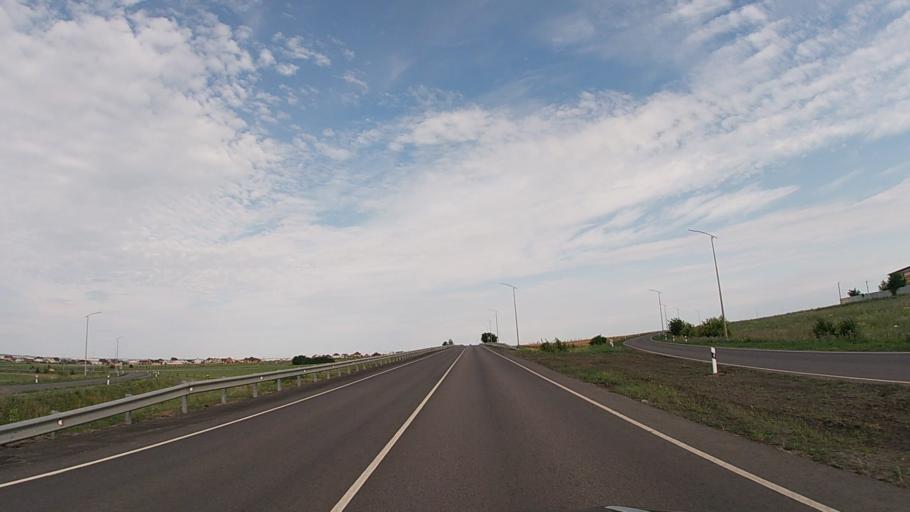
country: RU
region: Belgorod
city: Severnyy
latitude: 50.6734
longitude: 36.4770
